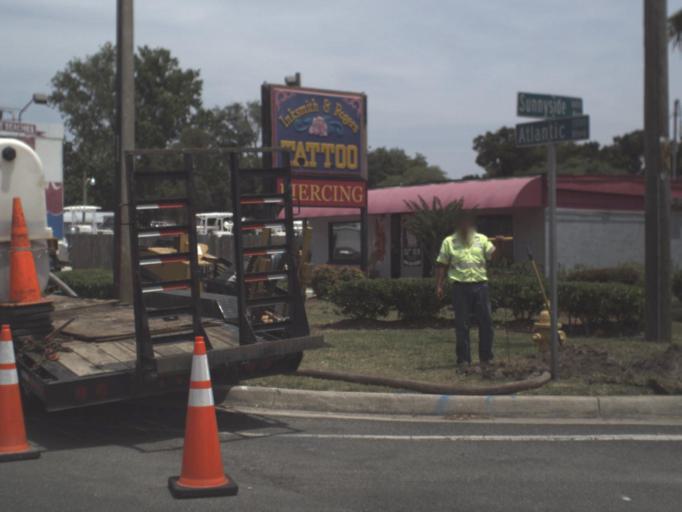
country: US
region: Florida
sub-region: Duval County
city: Atlantic Beach
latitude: 30.3219
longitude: -81.4452
